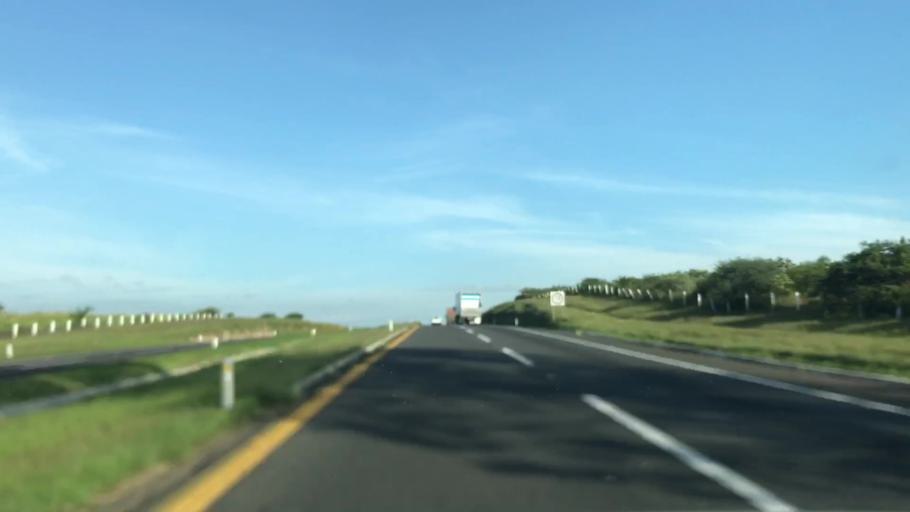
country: MX
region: Jalisco
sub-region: Union de San Antonio
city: San Jose del Caliche (El Caliche)
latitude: 21.2247
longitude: -101.9235
